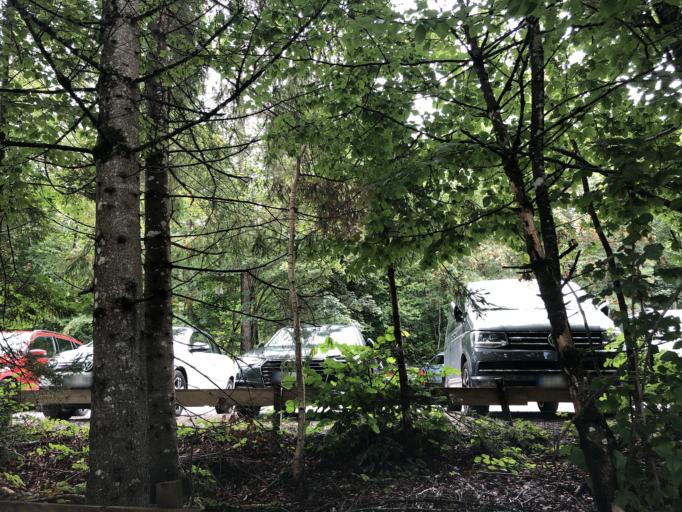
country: AT
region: Tyrol
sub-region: Politischer Bezirk Kufstein
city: Scheffau am Wilden Kaiser
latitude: 47.5424
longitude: 12.2246
